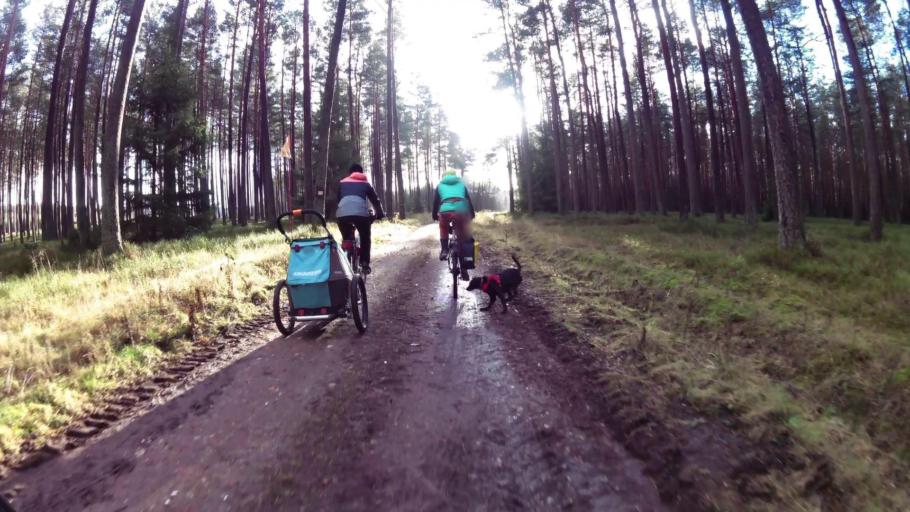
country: PL
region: West Pomeranian Voivodeship
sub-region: Powiat koszalinski
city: Sianow
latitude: 54.0886
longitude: 16.2933
